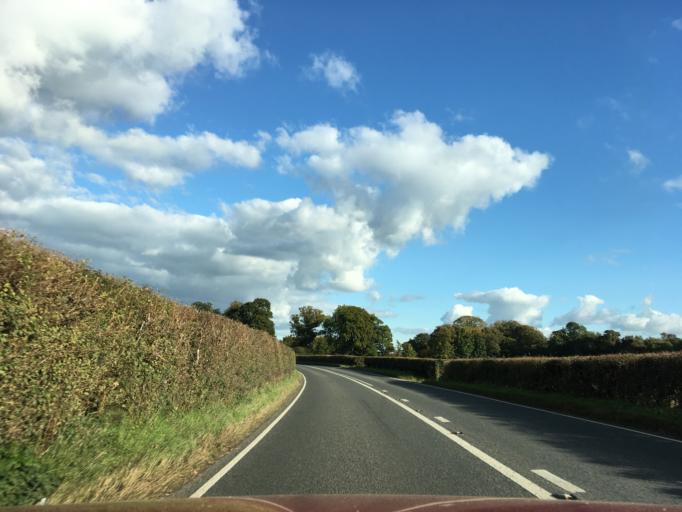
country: GB
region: England
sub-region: Herefordshire
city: Credenhill
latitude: 52.0742
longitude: -2.8328
